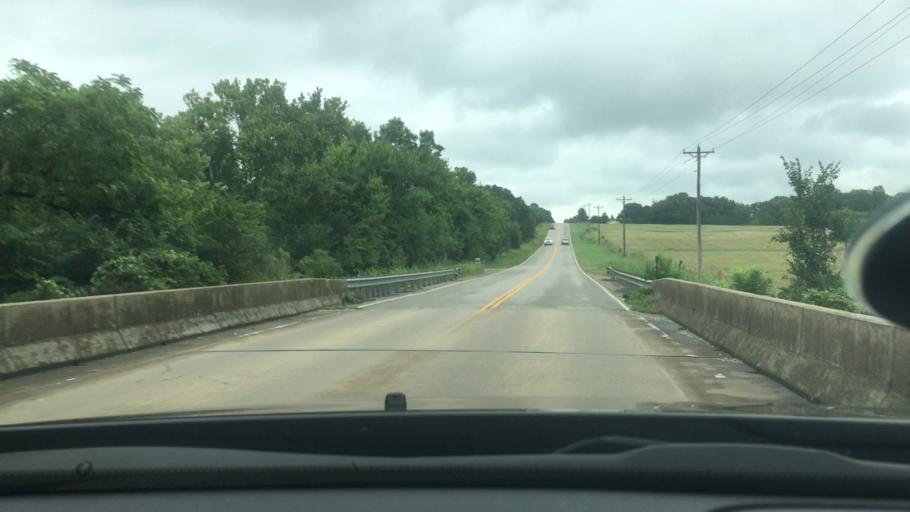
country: US
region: Oklahoma
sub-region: Bryan County
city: Calera
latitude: 33.9755
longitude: -96.5005
